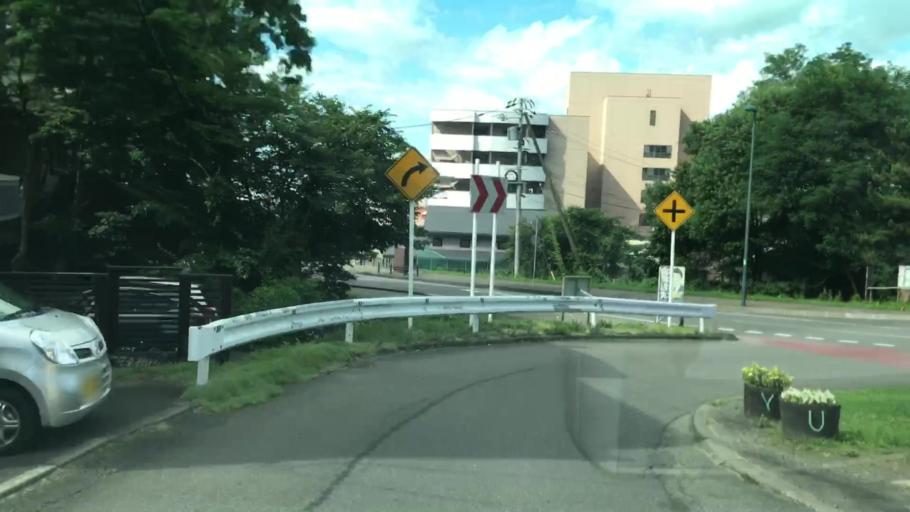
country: JP
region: Hokkaido
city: Muroran
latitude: 42.3122
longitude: 140.9763
